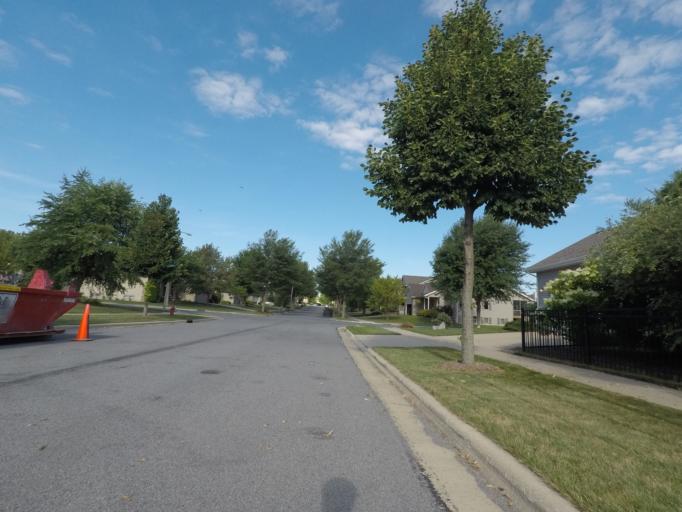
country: US
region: Wisconsin
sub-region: Dane County
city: Middleton
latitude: 43.0701
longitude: -89.5482
